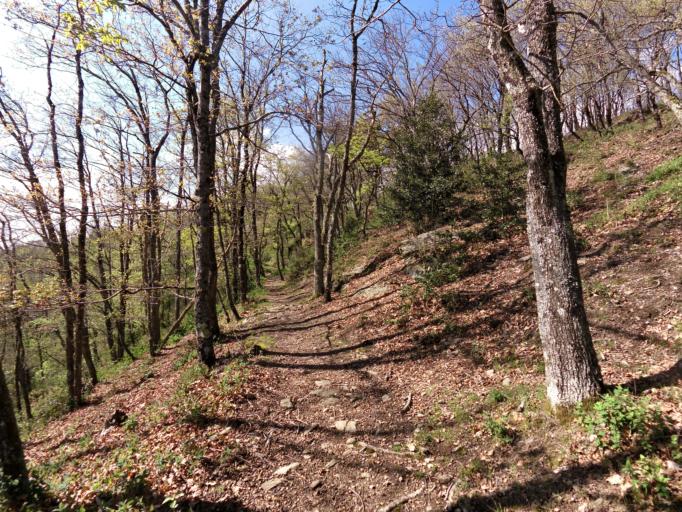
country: FR
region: Midi-Pyrenees
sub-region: Departement du Tarn
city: Soreze
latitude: 43.3750
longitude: 2.0776
